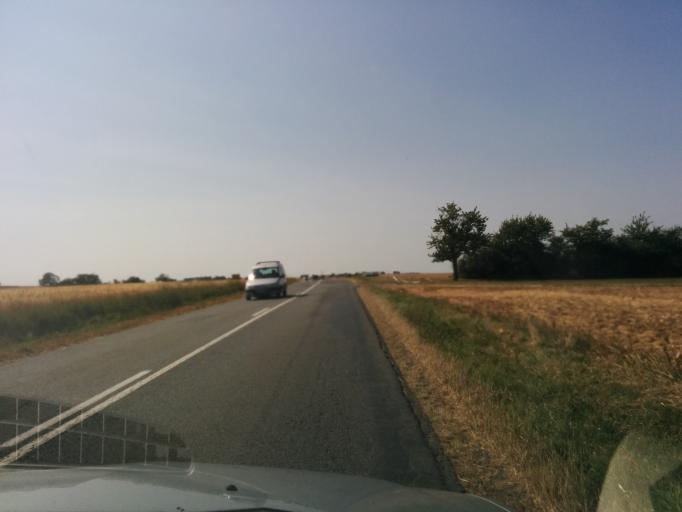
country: FR
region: Poitou-Charentes
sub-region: Departement de la Vienne
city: Mirebeau
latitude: 46.7874
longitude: 0.1238
